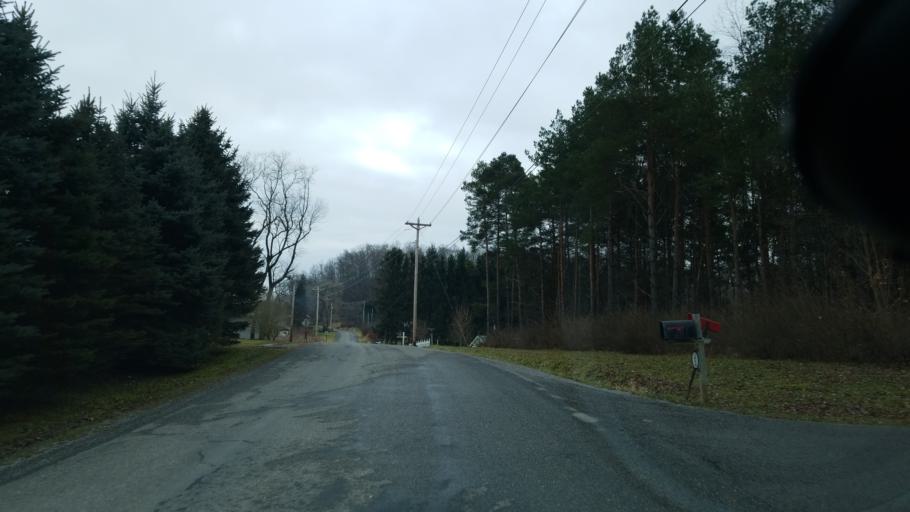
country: US
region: Pennsylvania
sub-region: Clearfield County
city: Treasure Lake
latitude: 41.1346
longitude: -78.6830
